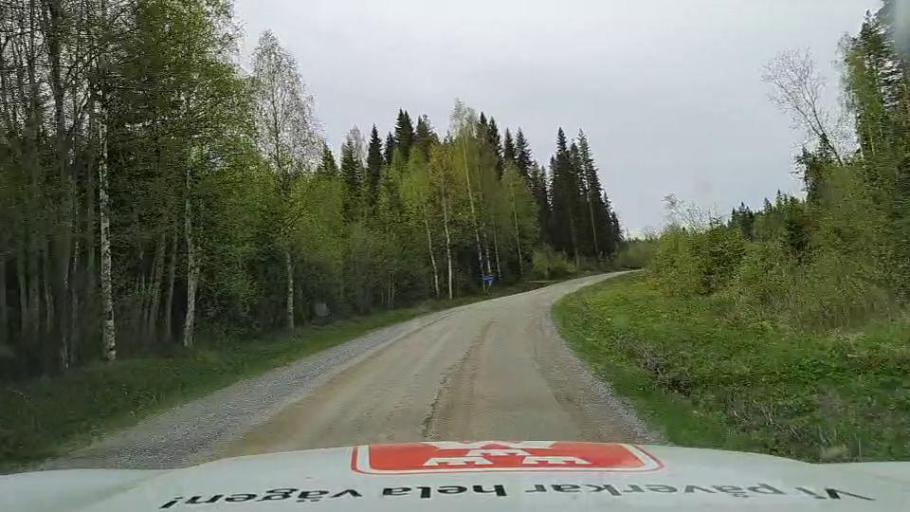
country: SE
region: Jaemtland
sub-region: Bergs Kommun
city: Hoverberg
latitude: 62.5333
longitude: 14.9089
